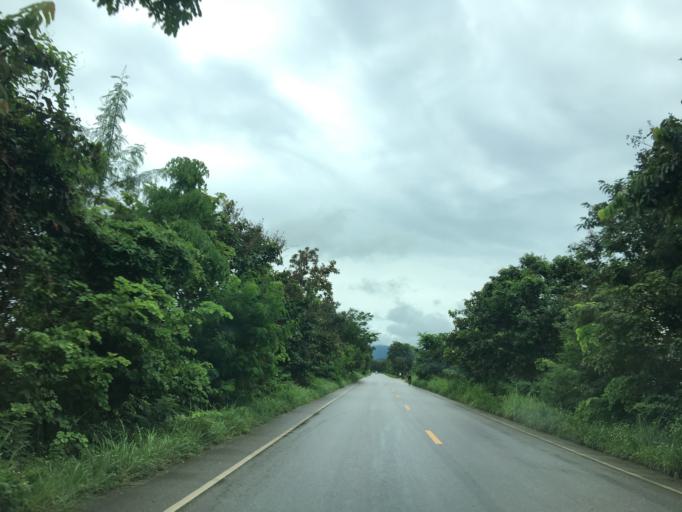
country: TH
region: Chiang Rai
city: Pa Daet
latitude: 19.4981
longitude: 99.9790
